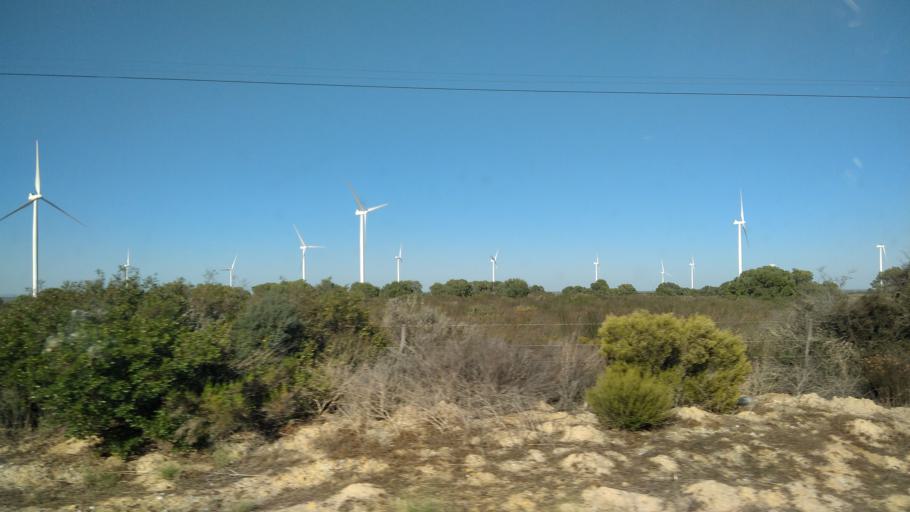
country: ZA
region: Western Cape
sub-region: West Coast District Municipality
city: Moorreesburg
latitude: -33.0810
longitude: 18.3898
